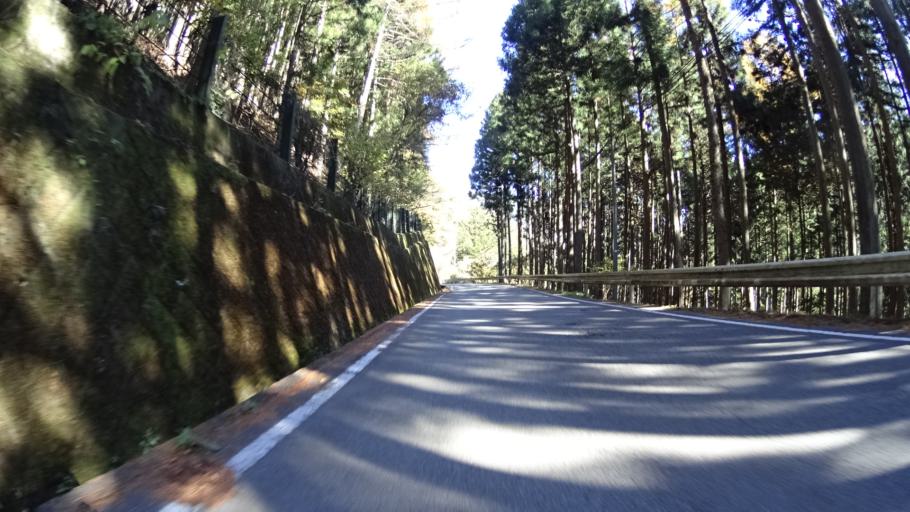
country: JP
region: Yamanashi
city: Otsuki
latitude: 35.7816
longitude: 138.9195
